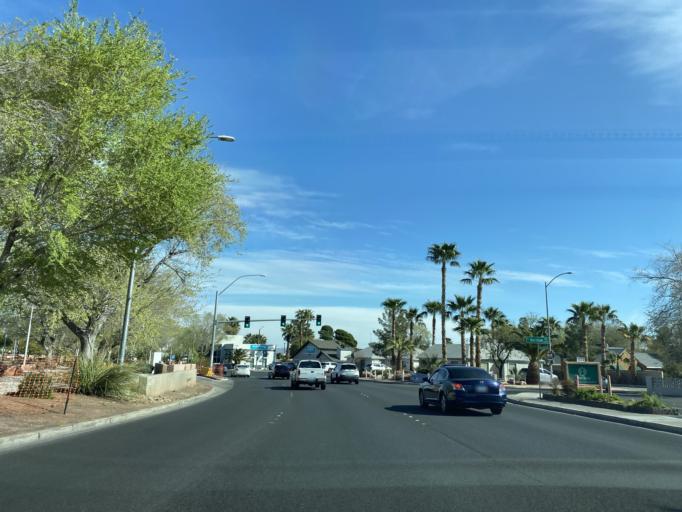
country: US
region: Nevada
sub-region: Clark County
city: Las Vegas
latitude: 36.1554
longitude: -115.1367
